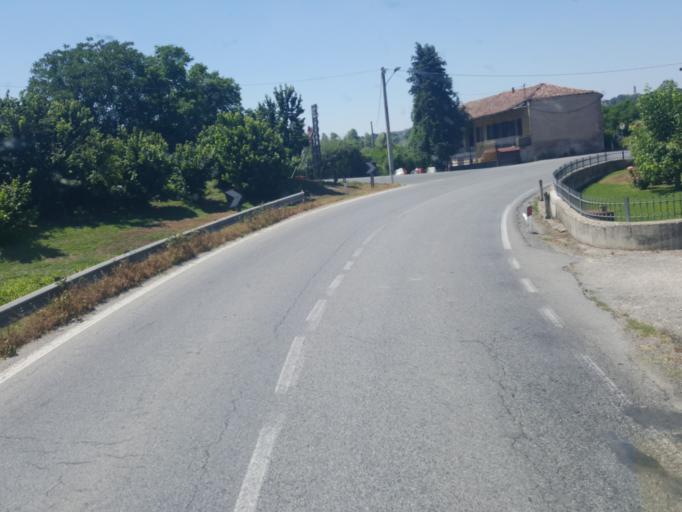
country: IT
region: Piedmont
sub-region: Provincia di Cuneo
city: Cherasco
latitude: 44.6570
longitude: 7.8568
